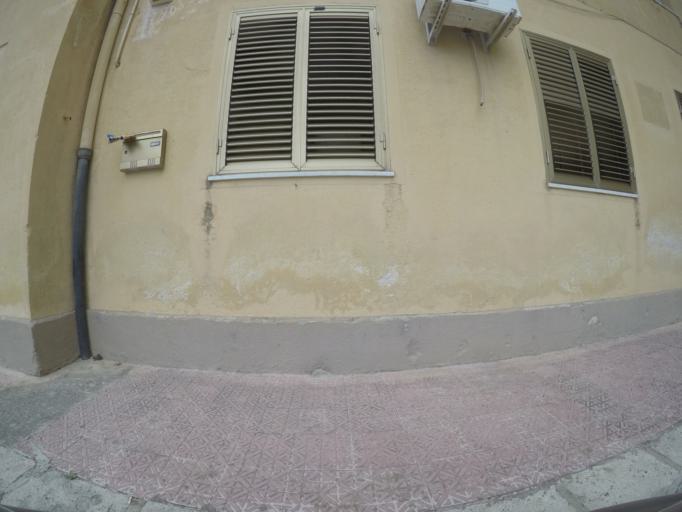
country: IT
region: Sicily
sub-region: Palermo
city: Giardinello
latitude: 38.0893
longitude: 13.1583
